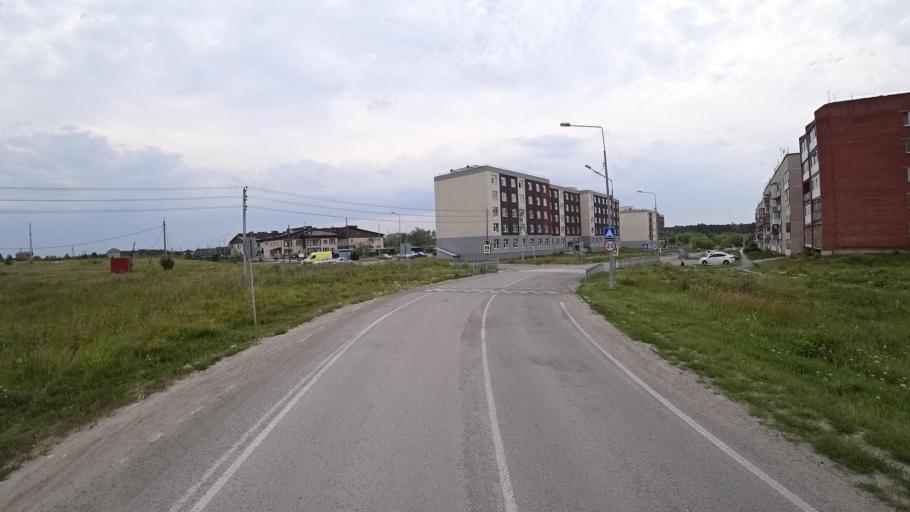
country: RU
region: Sverdlovsk
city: Kamyshlov
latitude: 56.8477
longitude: 62.7445
